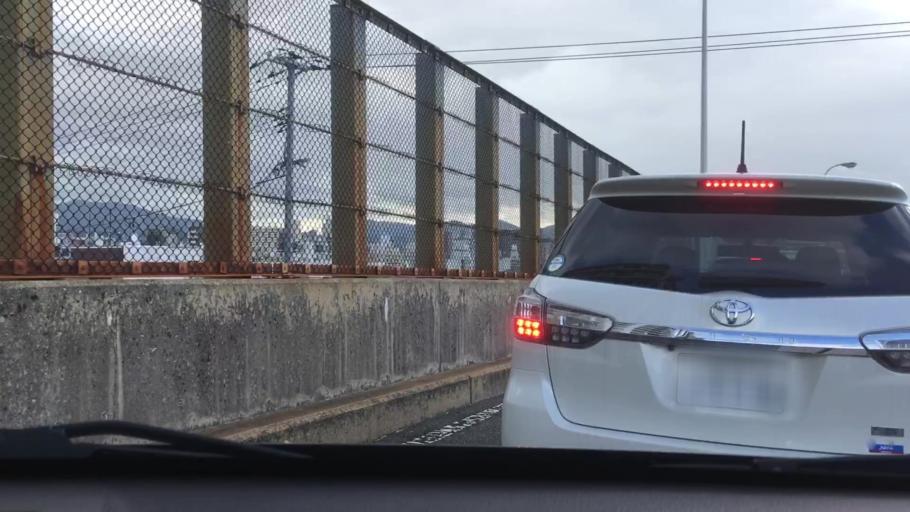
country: JP
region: Hiroshima
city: Hiroshima-shi
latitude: 34.4002
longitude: 132.4306
